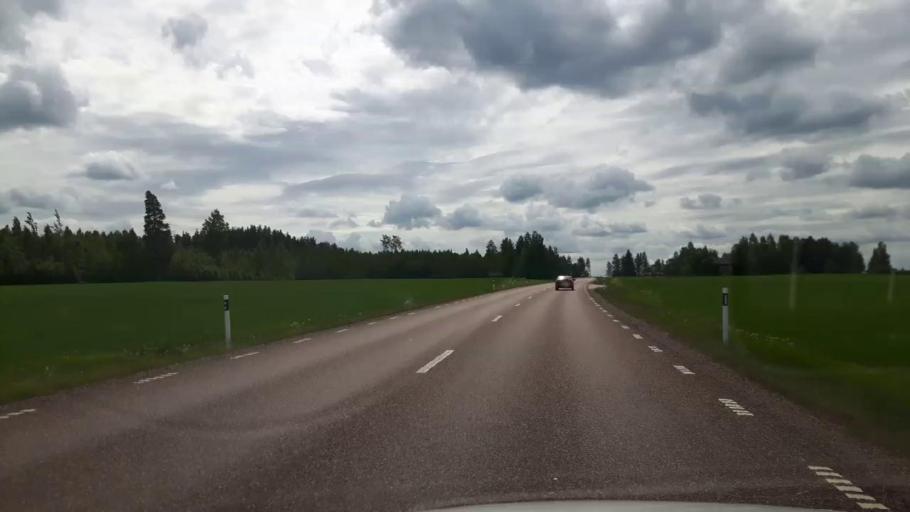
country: SE
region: Dalarna
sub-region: Hedemora Kommun
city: Hedemora
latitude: 60.3410
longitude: 15.9457
